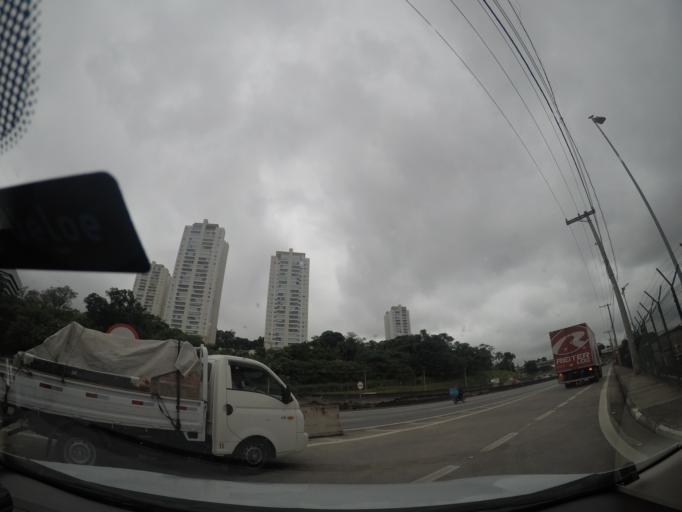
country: BR
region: Sao Paulo
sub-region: Osasco
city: Osasco
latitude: -23.4981
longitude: -46.7552
